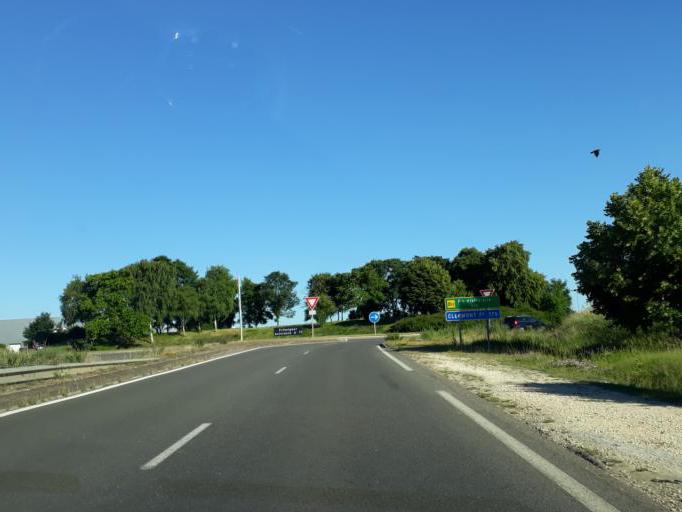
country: FR
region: Centre
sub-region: Departement du Cher
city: La Chapelle-Saint-Ursin
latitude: 47.0476
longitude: 2.3430
